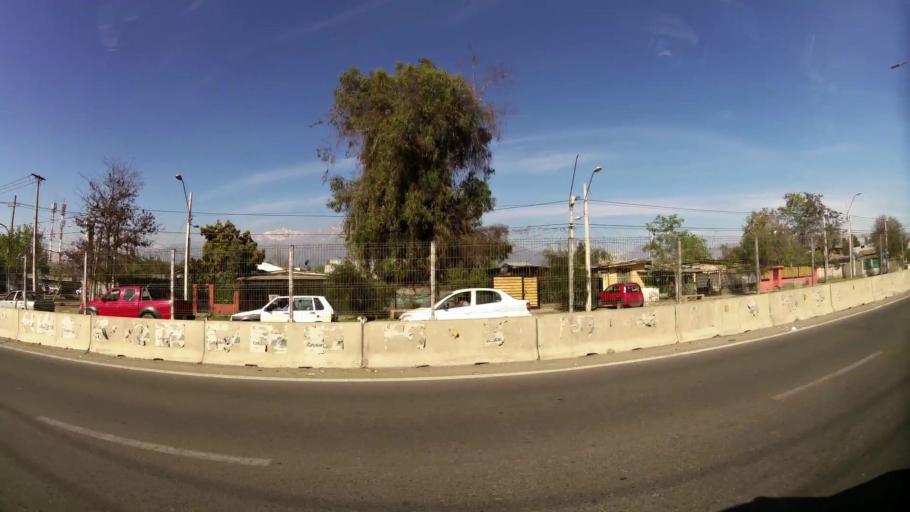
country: CL
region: Santiago Metropolitan
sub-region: Provincia de Santiago
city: La Pintana
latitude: -33.5383
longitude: -70.6207
